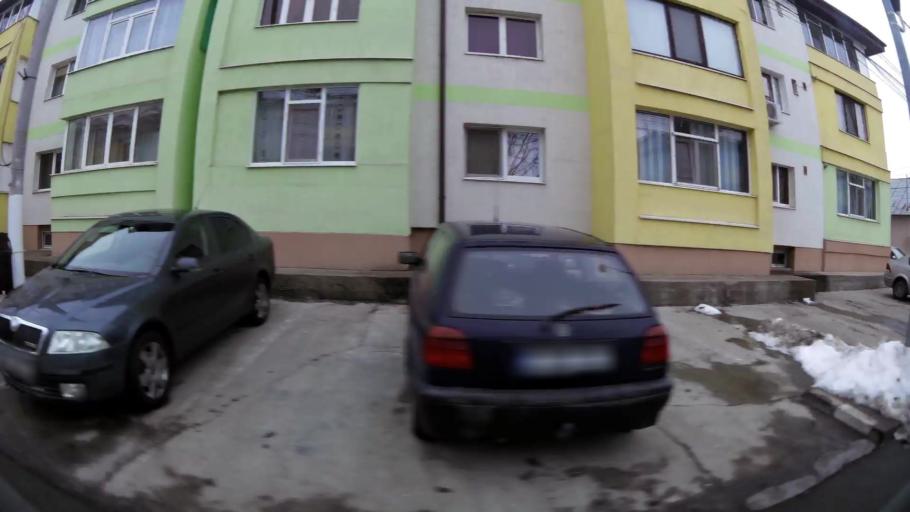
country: RO
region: Ilfov
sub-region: Comuna Pantelimon
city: Pantelimon
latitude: 44.4491
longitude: 26.2032
